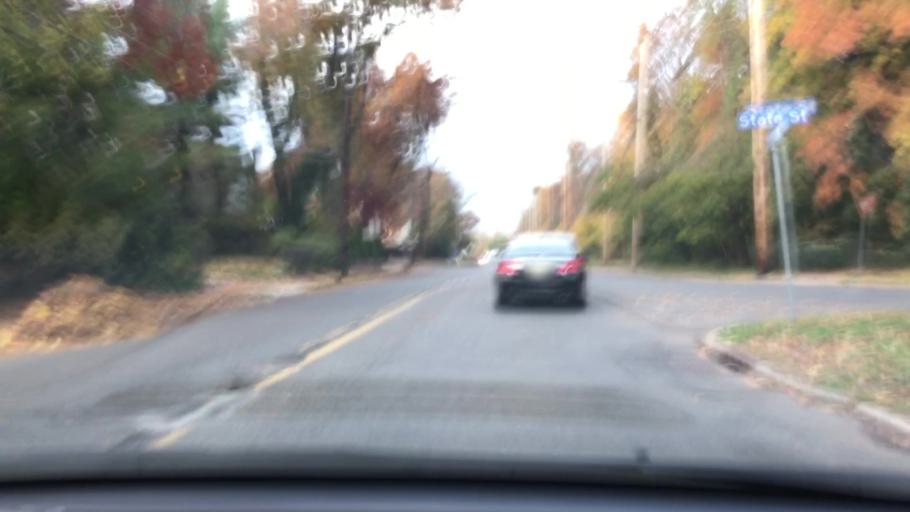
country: US
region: New Jersey
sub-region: Bergen County
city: Teaneck
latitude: 40.9048
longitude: -74.0064
